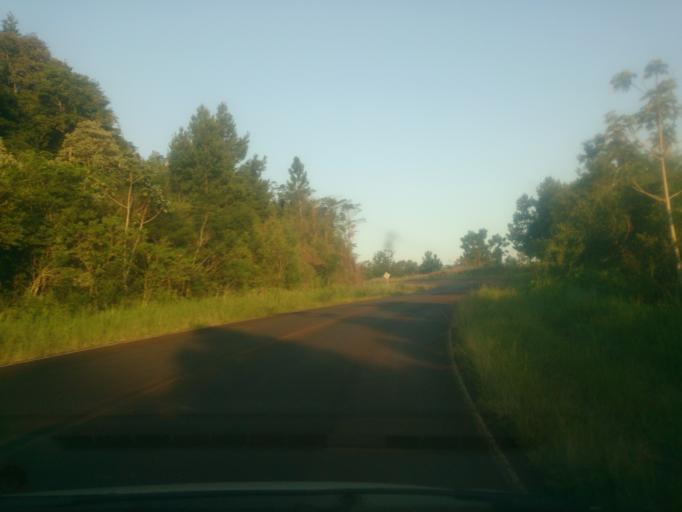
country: AR
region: Misiones
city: Panambi
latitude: -27.6641
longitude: -54.9136
